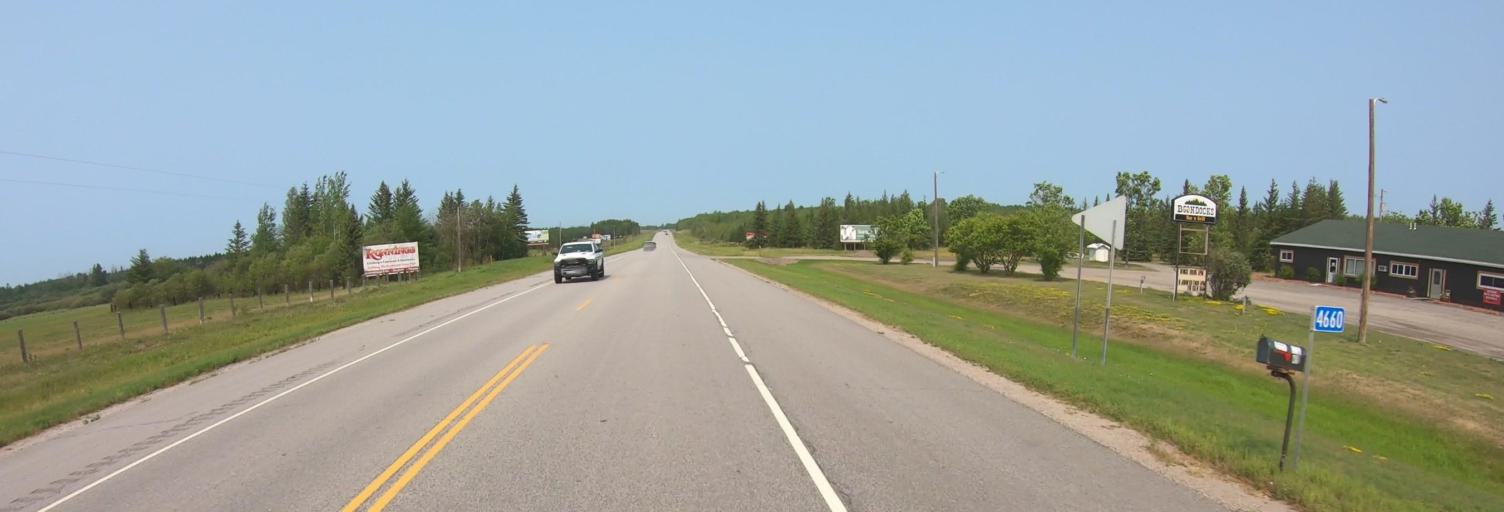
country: CA
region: Ontario
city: Fort Frances
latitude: 48.4130
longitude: -93.2066
